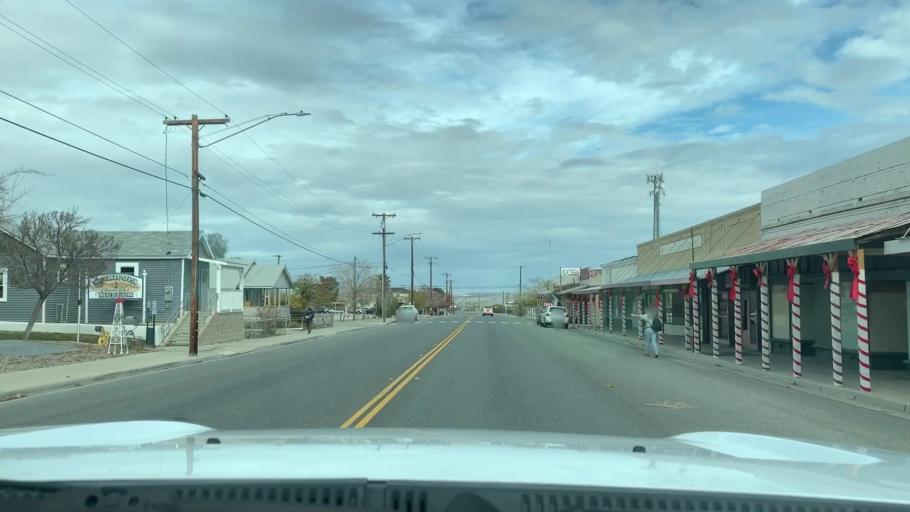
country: US
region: California
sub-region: Kern County
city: Maricopa
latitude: 35.0627
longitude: -119.4017
